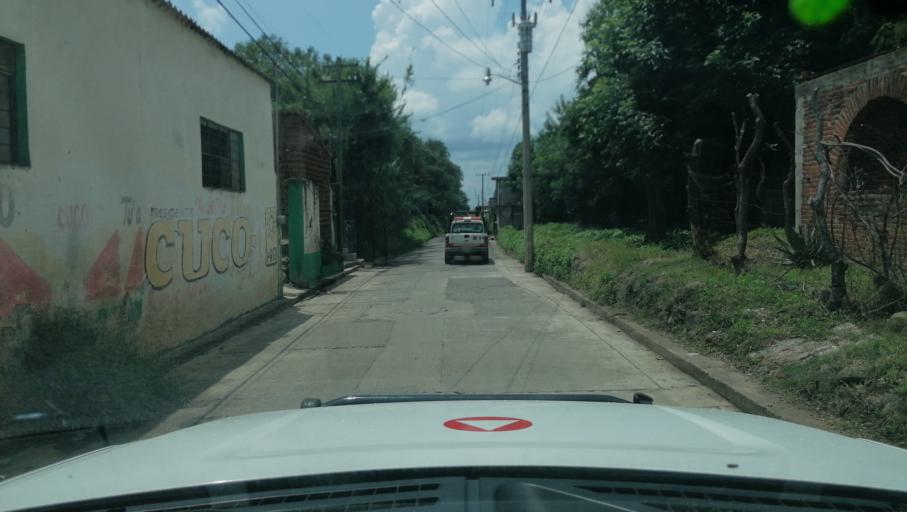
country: MX
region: Morelos
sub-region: Yecapixtla
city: Yecapixtla
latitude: 18.8818
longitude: -98.8213
